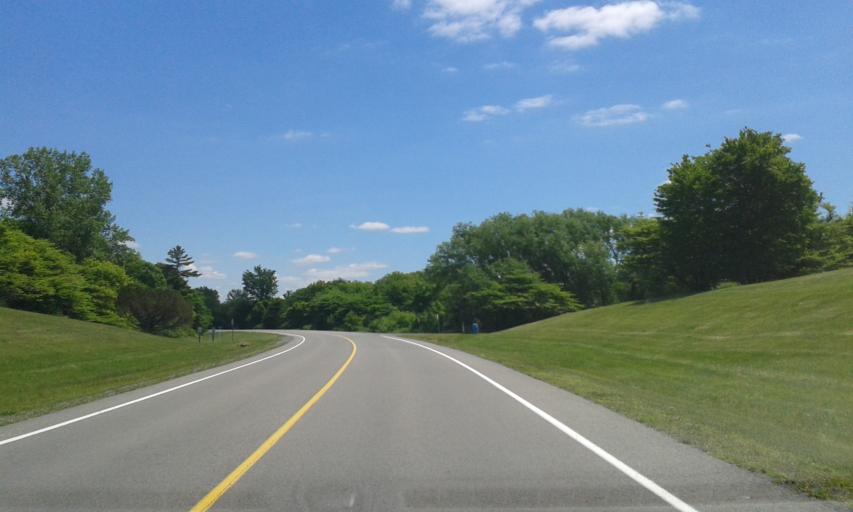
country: US
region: New York
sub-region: St. Lawrence County
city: Massena
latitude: 44.9941
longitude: -74.9329
